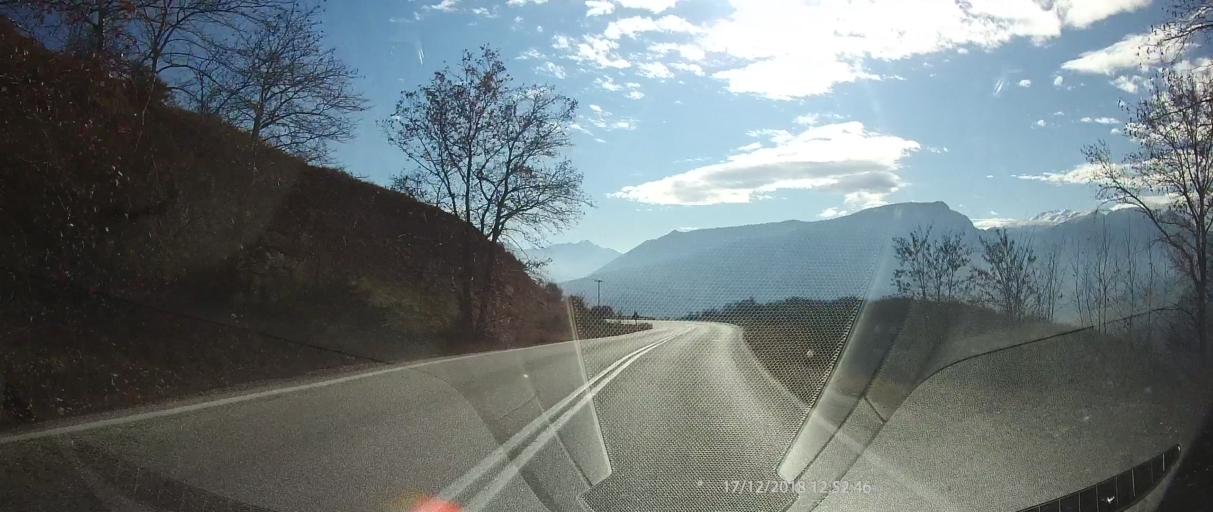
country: GR
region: Thessaly
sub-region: Trikala
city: Kastraki
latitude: 39.7577
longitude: 21.4829
